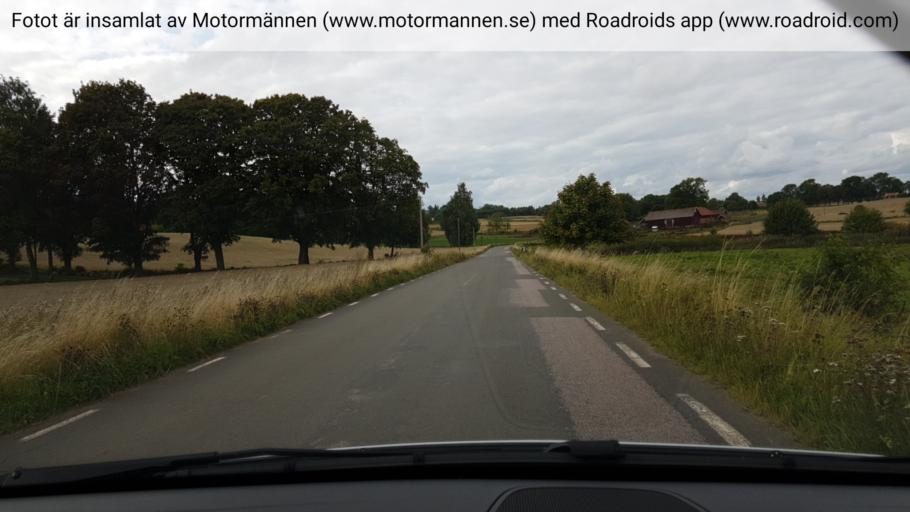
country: SE
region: Vaestra Goetaland
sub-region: Skovde Kommun
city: Skultorp
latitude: 58.2303
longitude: 13.7986
